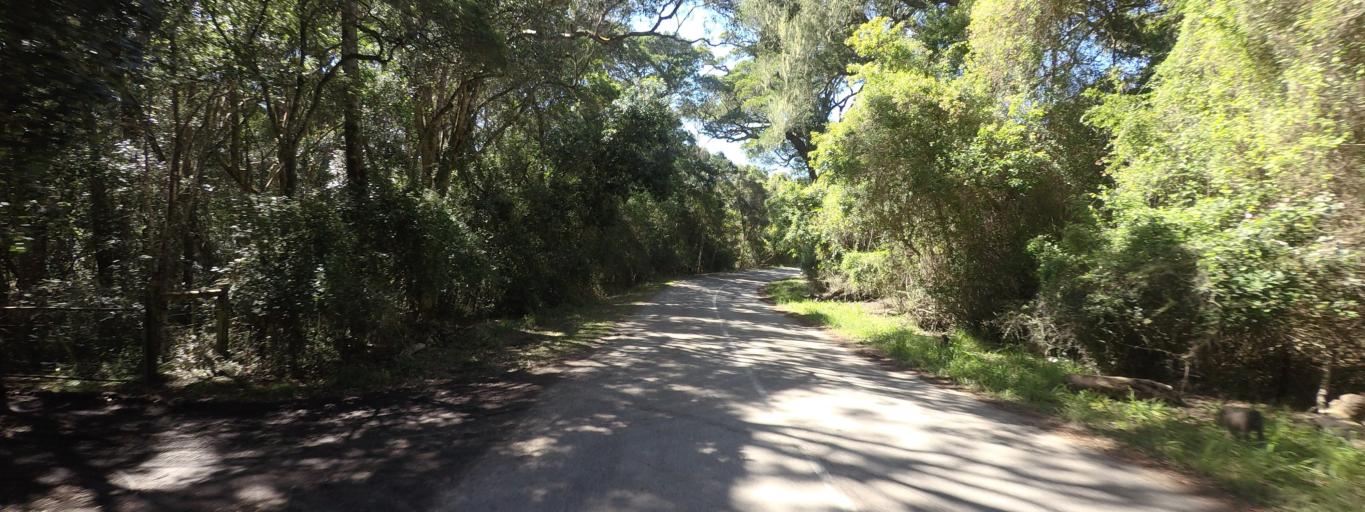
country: ZA
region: Western Cape
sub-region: Eden District Municipality
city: Plettenberg Bay
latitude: -33.9698
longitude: 23.5611
